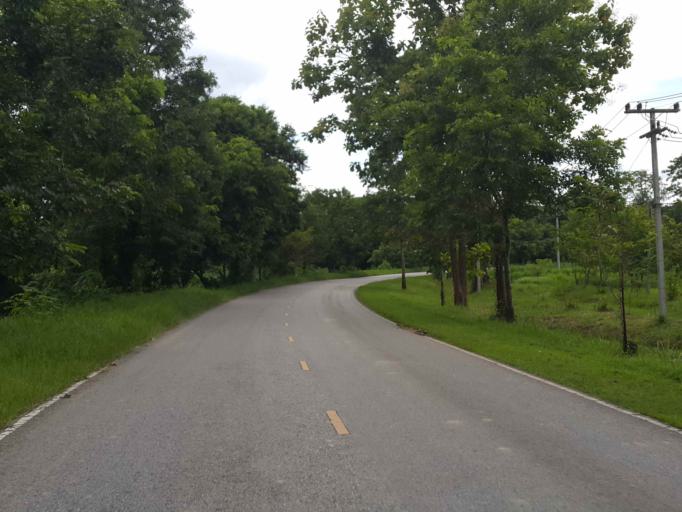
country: TH
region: Chiang Mai
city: Chiang Mai
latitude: 18.8968
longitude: 98.9390
